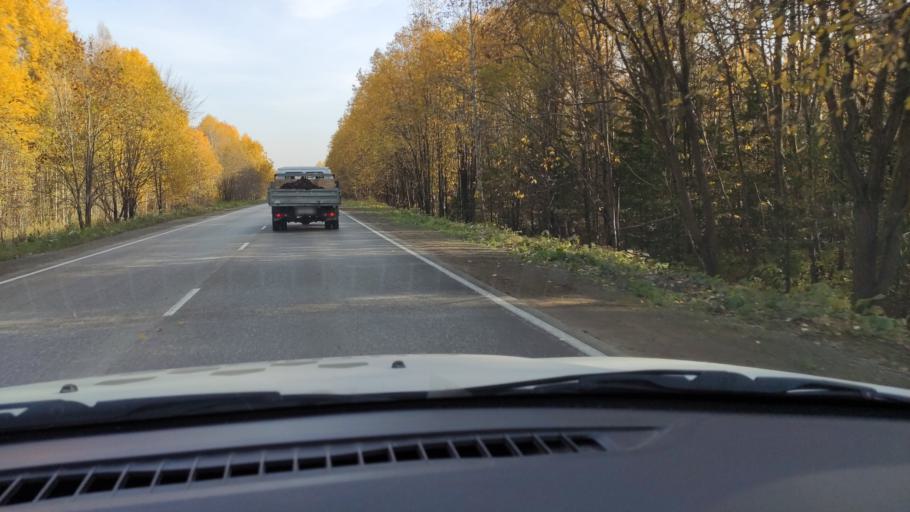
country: RU
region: Perm
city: Novyye Lyady
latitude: 58.0226
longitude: 56.6604
